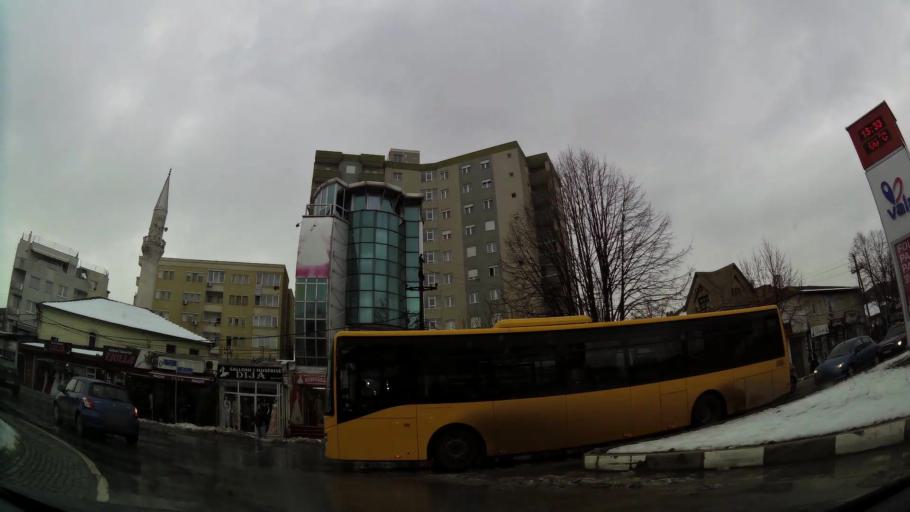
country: XK
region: Pristina
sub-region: Komuna e Prishtines
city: Pristina
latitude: 42.6674
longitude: 21.1642
